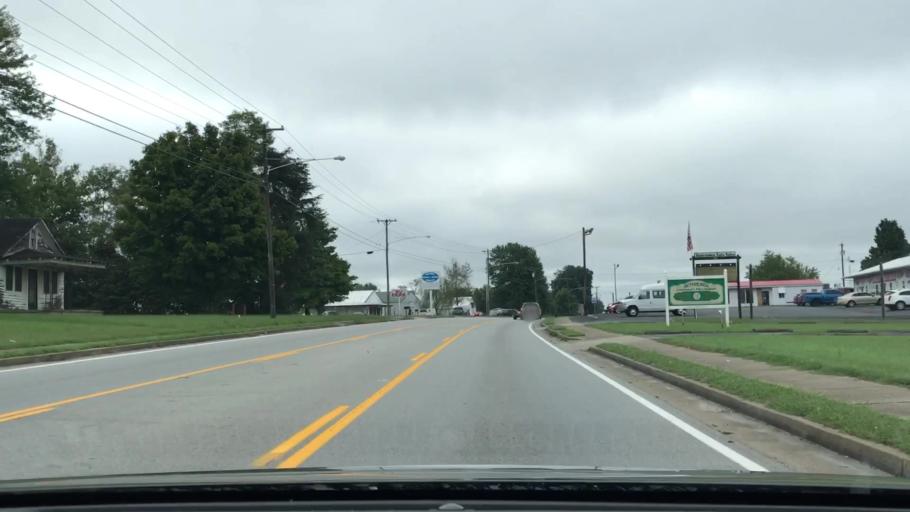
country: US
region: Kentucky
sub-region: Russell County
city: Russell Springs
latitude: 37.0224
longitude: -85.0763
